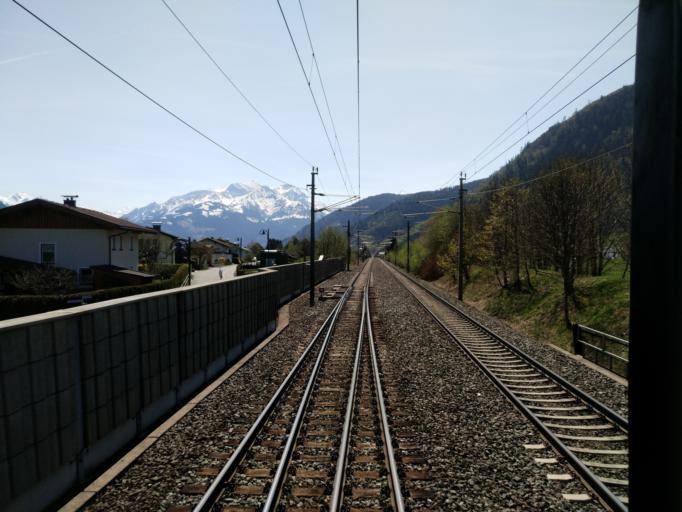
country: AT
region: Salzburg
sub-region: Politischer Bezirk Zell am See
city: Maishofen
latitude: 47.3555
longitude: 12.8084
